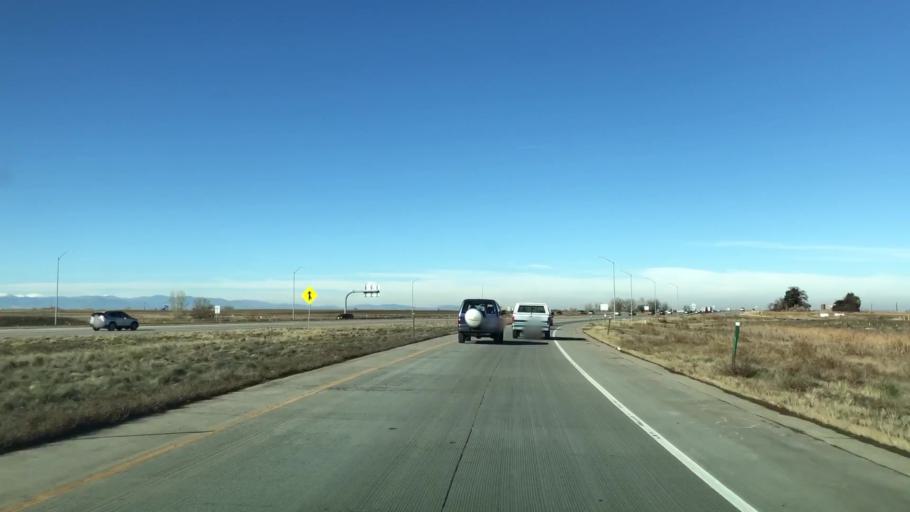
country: US
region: Colorado
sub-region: Weld County
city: Dacono
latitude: 40.0901
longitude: -104.9797
